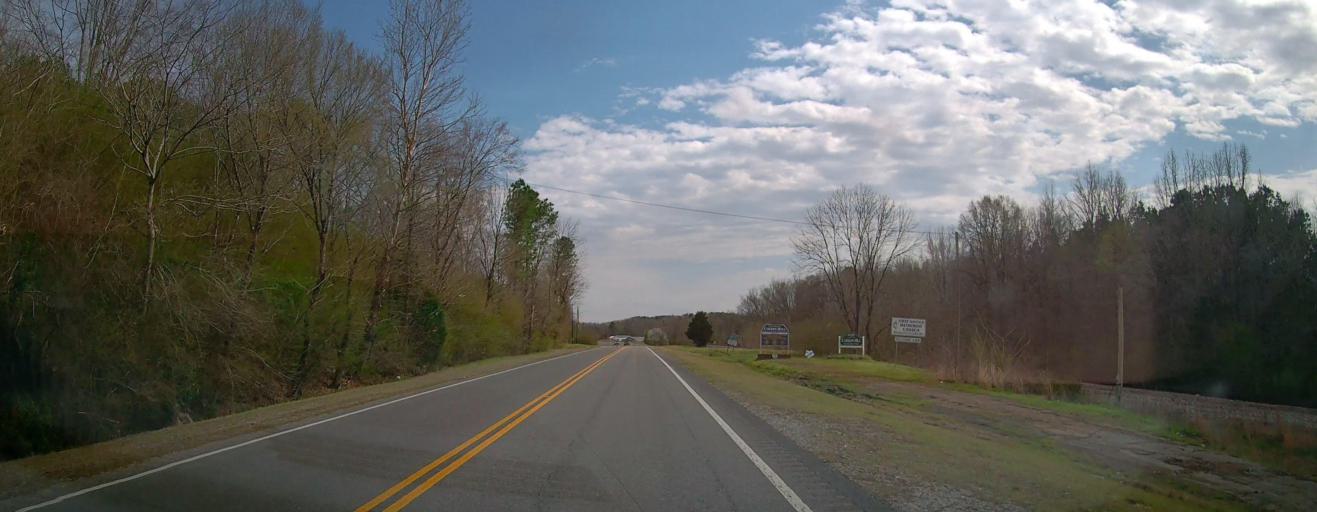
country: US
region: Alabama
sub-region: Walker County
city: Carbon Hill
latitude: 33.8945
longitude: -87.5360
